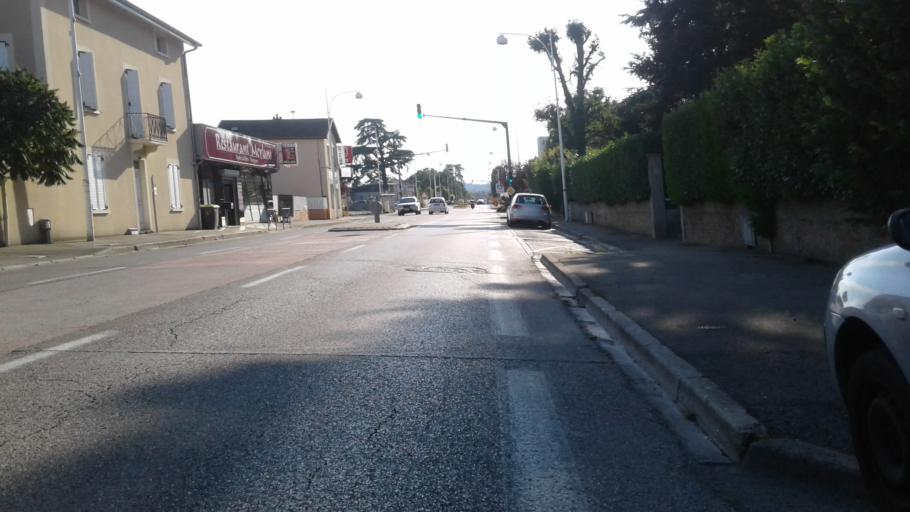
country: FR
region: Rhone-Alpes
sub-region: Departement de l'Ain
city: Saint-Maurice-de-Beynost
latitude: 45.8307
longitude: 4.9828
